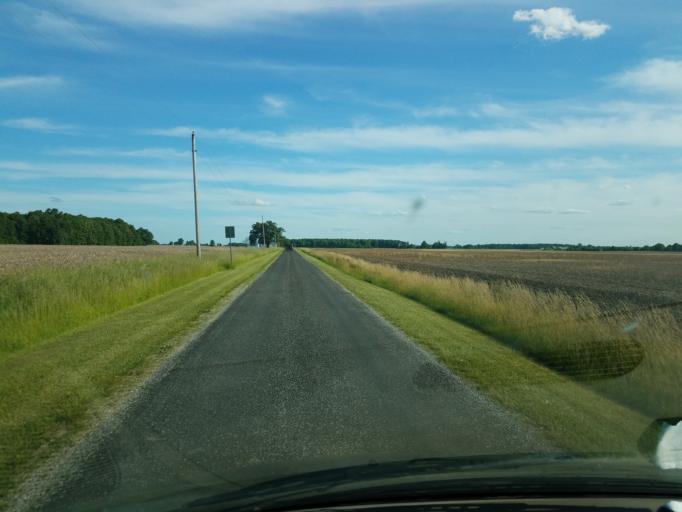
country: US
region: Ohio
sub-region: Morrow County
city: Cardington
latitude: 40.5247
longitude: -82.9862
